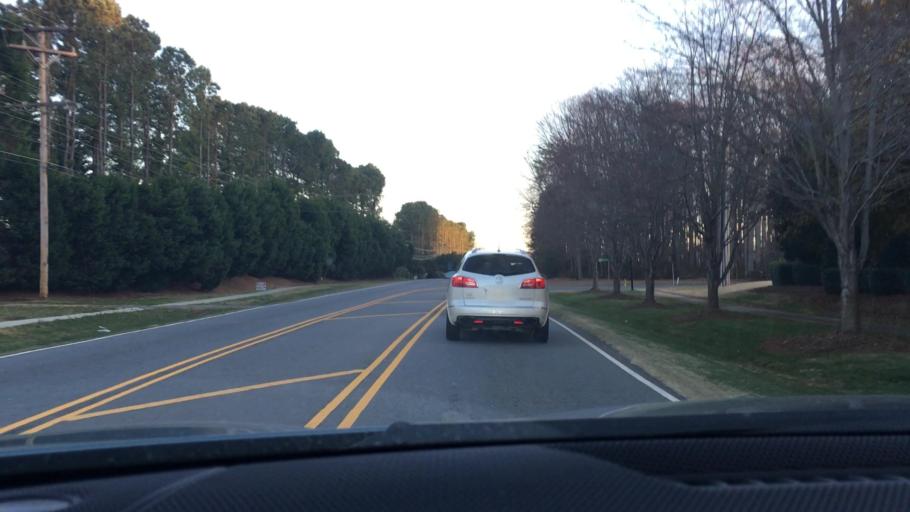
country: US
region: North Carolina
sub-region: Mecklenburg County
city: Cornelius
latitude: 35.4411
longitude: -80.8997
